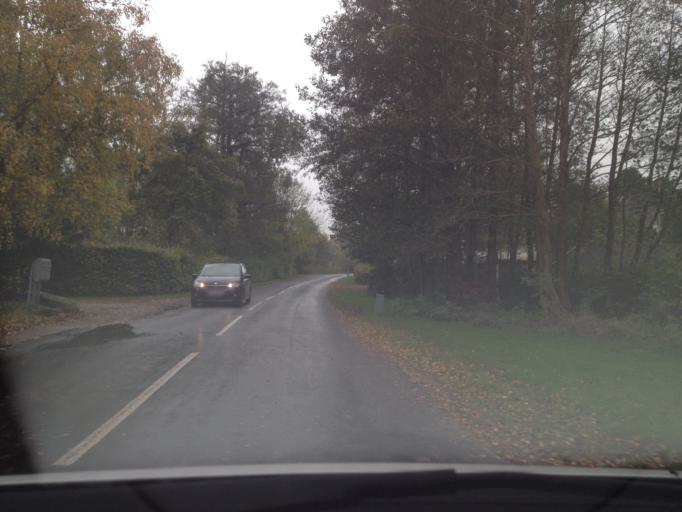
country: DK
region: Capital Region
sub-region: Hillerod Kommune
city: Nodebo
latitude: 55.9689
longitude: 12.3710
